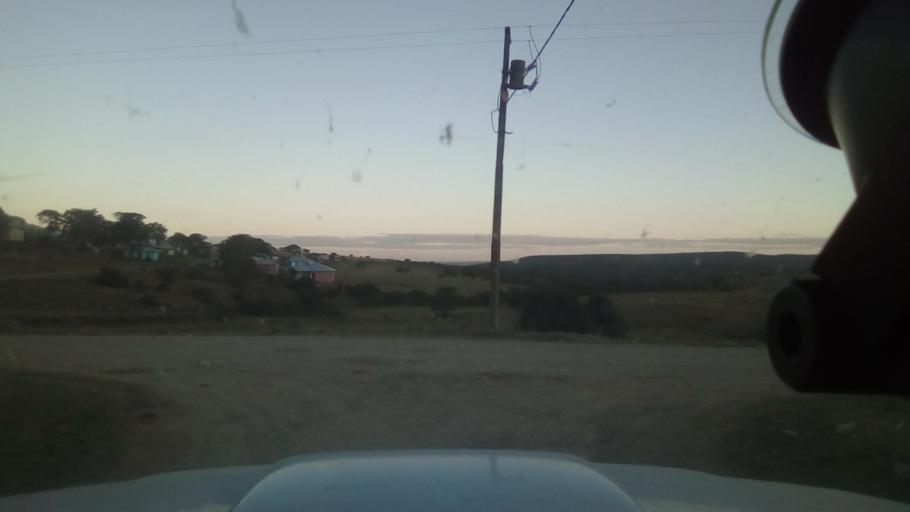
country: ZA
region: Eastern Cape
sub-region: Buffalo City Metropolitan Municipality
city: Bhisho
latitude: -32.7375
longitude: 27.3733
